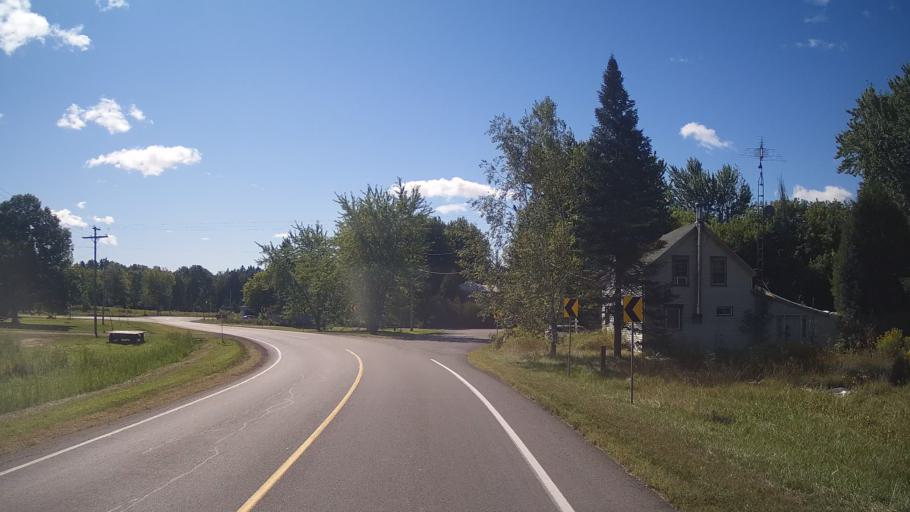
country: CA
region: Ontario
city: Prescott
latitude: 44.9026
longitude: -75.3996
